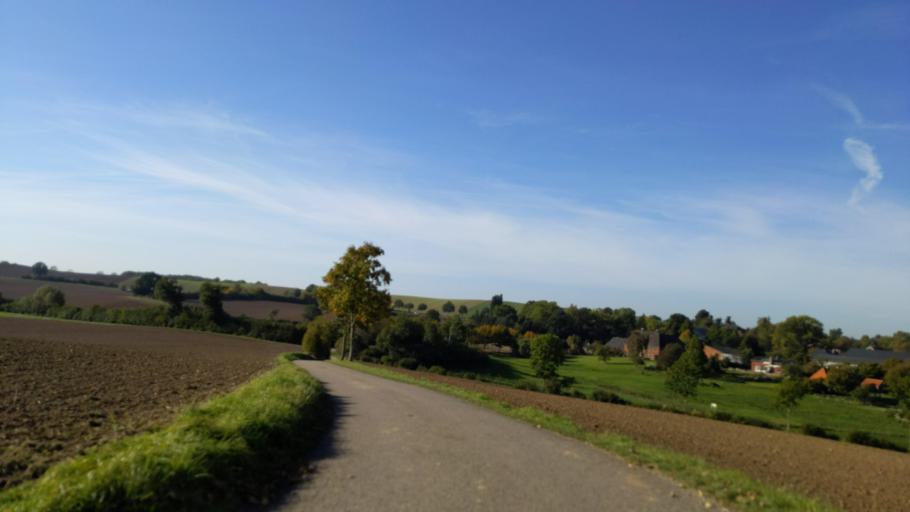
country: DE
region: Schleswig-Holstein
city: Ahrensbok
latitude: 54.0610
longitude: 10.5853
